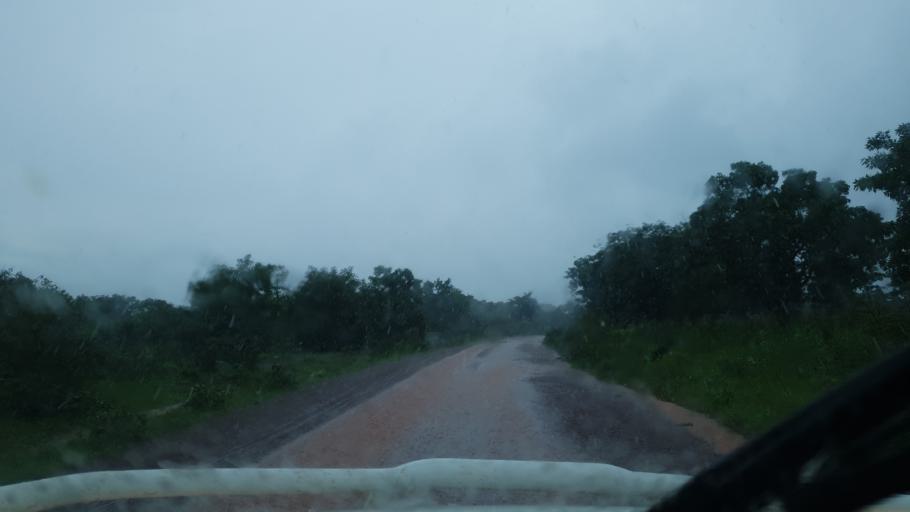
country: ML
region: Sikasso
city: Kolondieba
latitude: 11.6137
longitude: -6.6764
